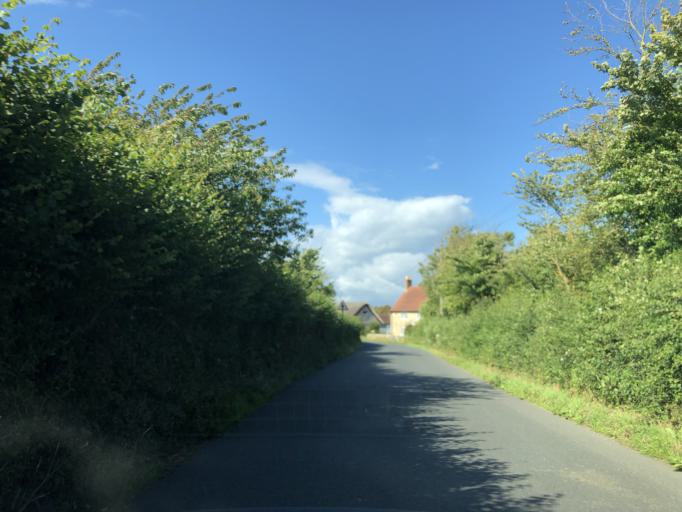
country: GB
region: England
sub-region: Isle of Wight
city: Shalfleet
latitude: 50.6849
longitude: -1.4002
